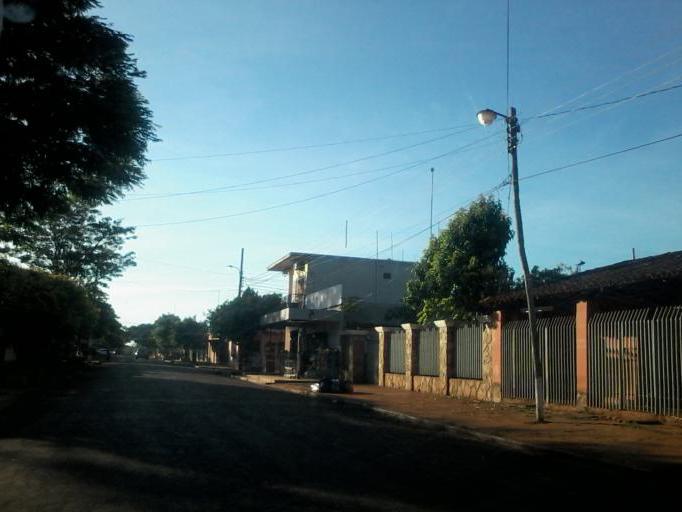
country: PY
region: Alto Parana
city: Ciudad del Este
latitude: -25.4352
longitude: -54.6422
